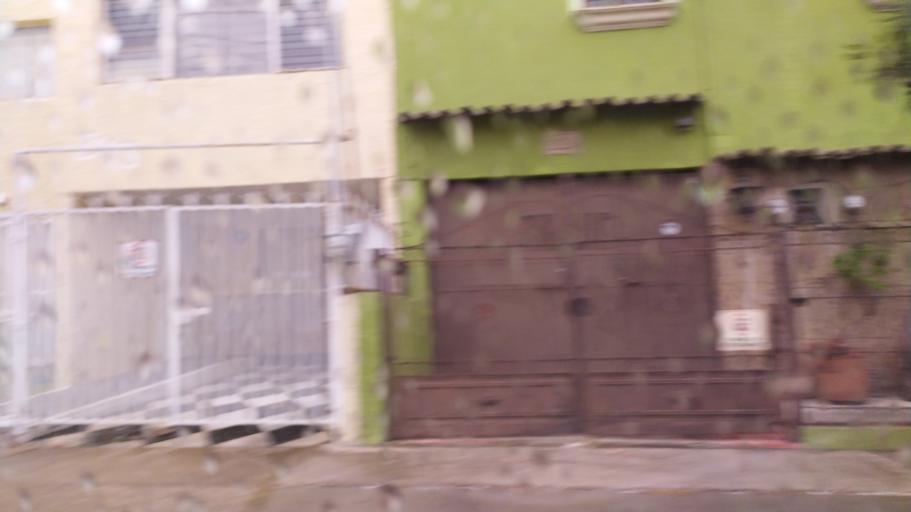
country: MX
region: Jalisco
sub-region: Zapopan
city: Zapopan
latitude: 20.7089
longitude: -103.3627
